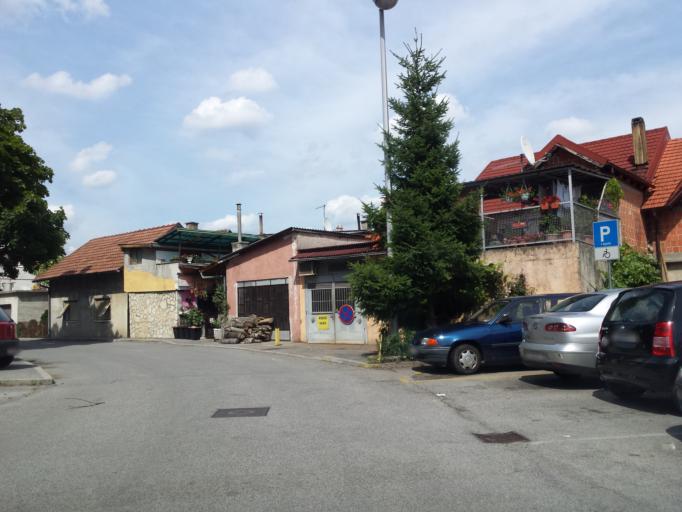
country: HR
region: Grad Zagreb
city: Jankomir
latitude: 45.7980
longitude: 15.9146
